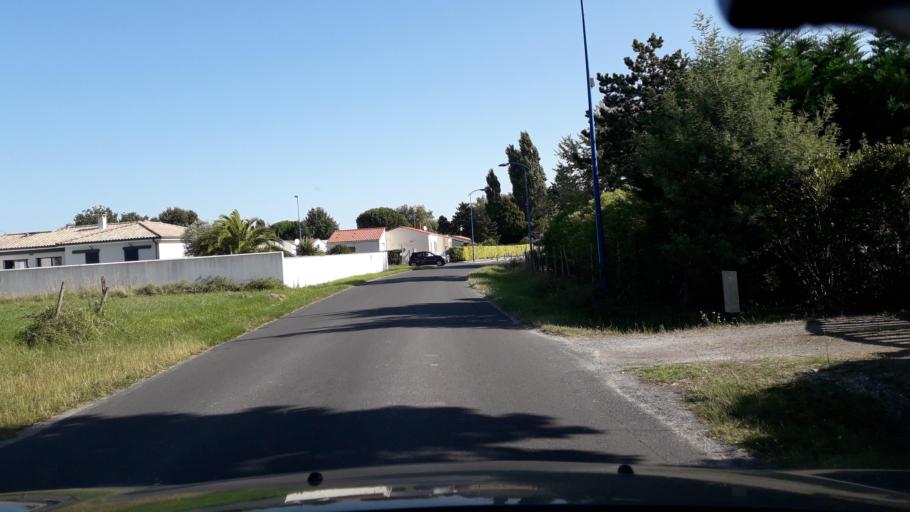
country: FR
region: Poitou-Charentes
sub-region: Departement de la Charente-Maritime
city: Etaules
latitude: 45.7211
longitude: -1.1045
